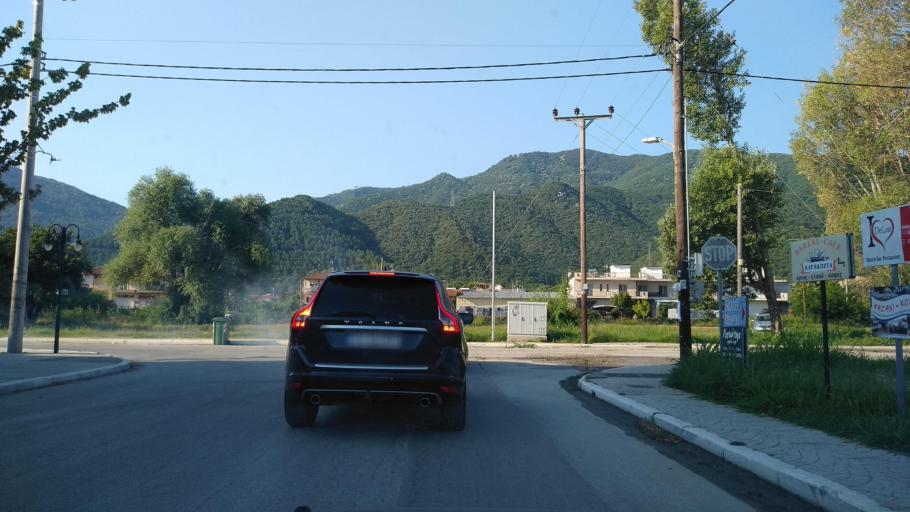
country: GR
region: Central Macedonia
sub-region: Nomos Thessalonikis
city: Stavros
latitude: 40.6669
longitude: 23.6911
